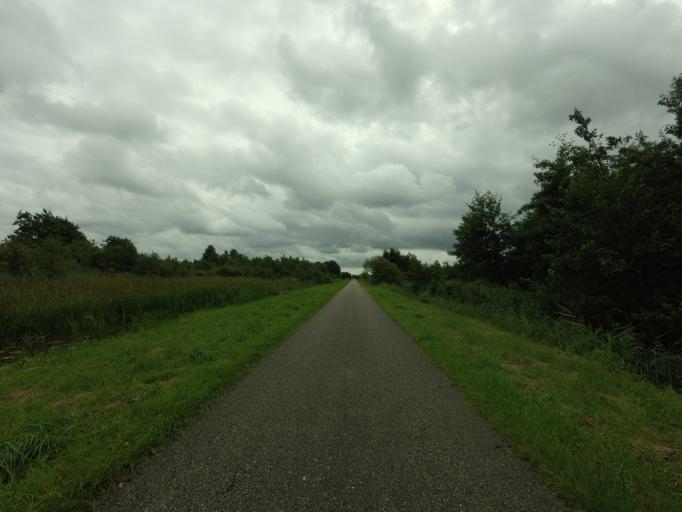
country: NL
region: Friesland
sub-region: Gemeente Weststellingwerf
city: Steggerda
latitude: 52.8687
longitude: 6.0598
